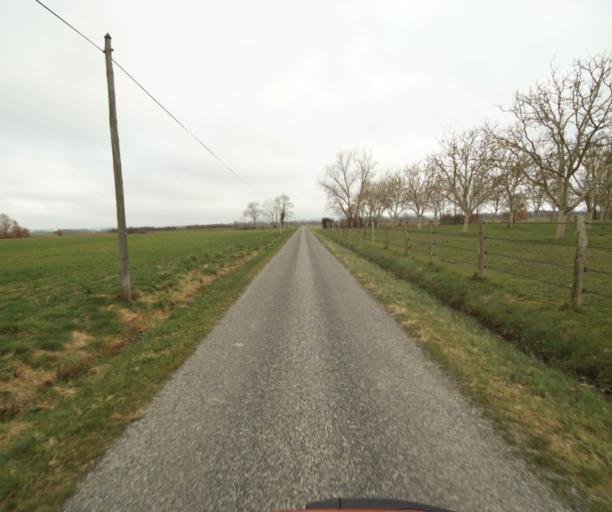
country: FR
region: Languedoc-Roussillon
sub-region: Departement de l'Aude
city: Belpech
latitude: 43.1812
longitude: 1.6876
